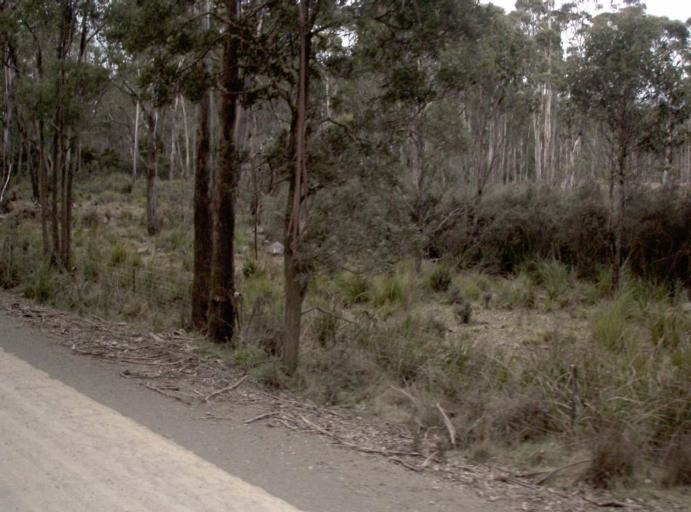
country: AU
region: Tasmania
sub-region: Launceston
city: Mayfield
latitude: -41.3524
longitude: 147.2208
